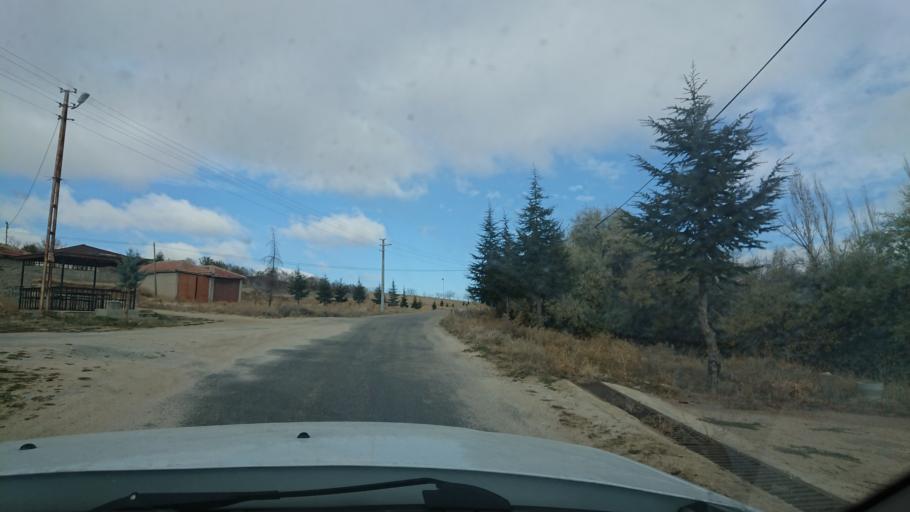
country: TR
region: Aksaray
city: Agacoren
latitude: 38.8242
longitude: 33.9580
